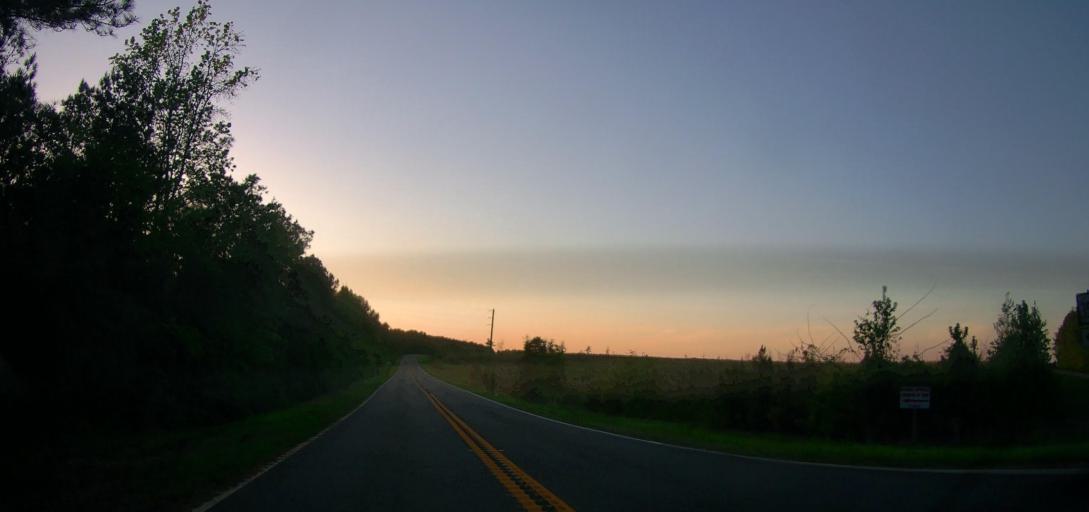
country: US
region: Georgia
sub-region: Marion County
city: Buena Vista
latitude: 32.3790
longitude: -84.5581
